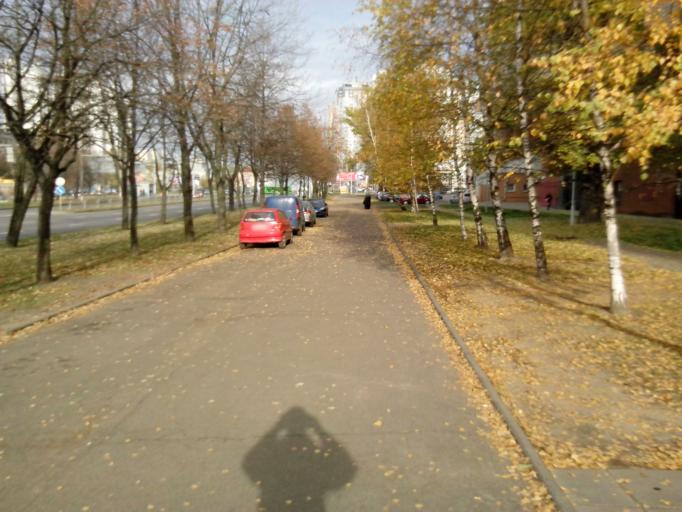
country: BY
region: Minsk
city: Minsk
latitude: 53.9343
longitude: 27.5809
